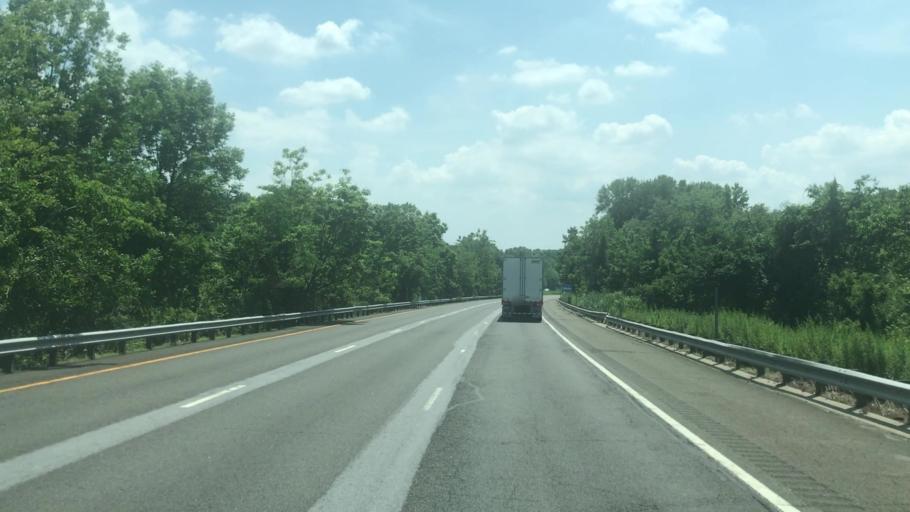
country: US
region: New York
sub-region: Westchester County
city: Armonk
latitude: 41.1569
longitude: -73.6895
